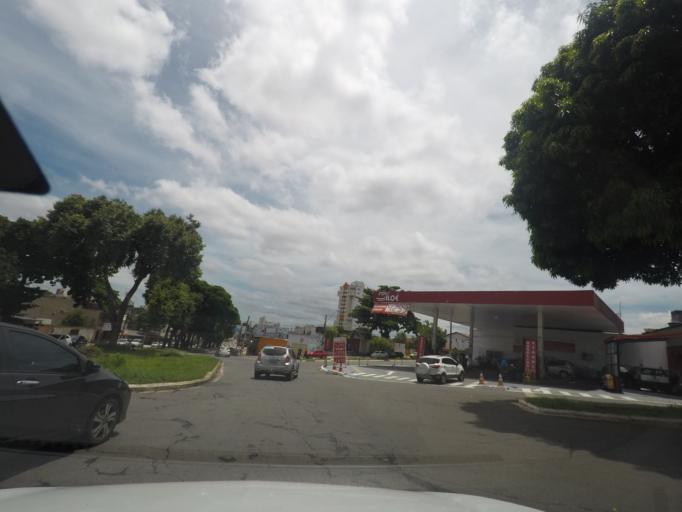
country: BR
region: Goias
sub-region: Goiania
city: Goiania
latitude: -16.6882
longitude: -49.2425
